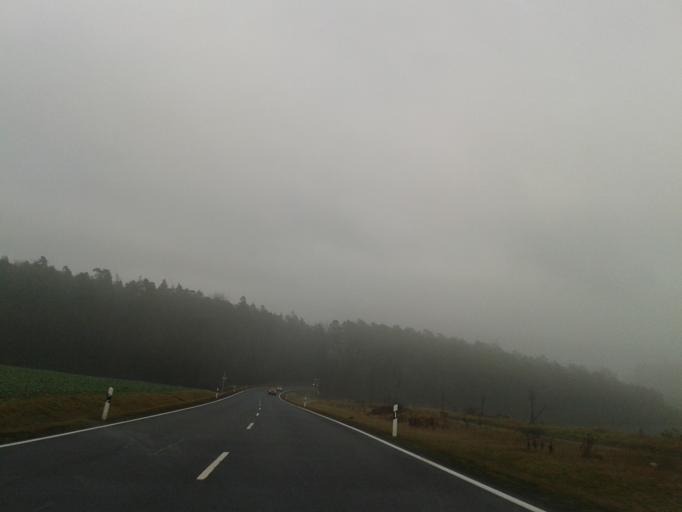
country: DE
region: Bavaria
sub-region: Regierungsbezirk Unterfranken
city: Pfarrweisach
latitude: 50.1833
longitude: 10.7206
